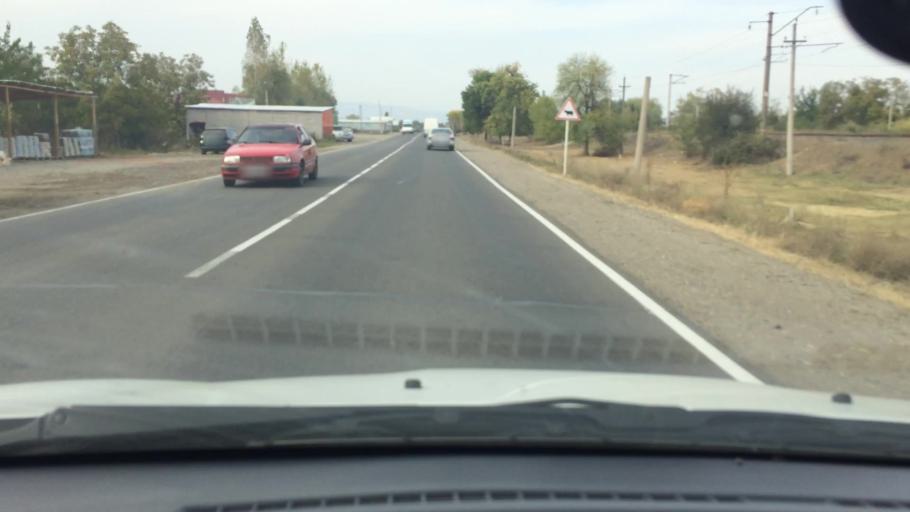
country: GE
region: Kvemo Kartli
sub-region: Marneuli
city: Marneuli
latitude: 41.4203
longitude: 44.8251
